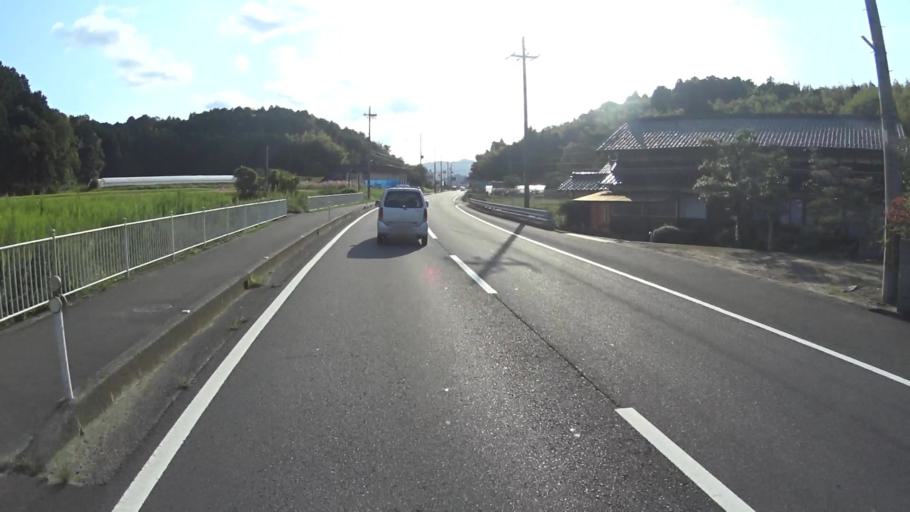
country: JP
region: Kyoto
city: Miyazu
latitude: 35.5251
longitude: 135.1159
